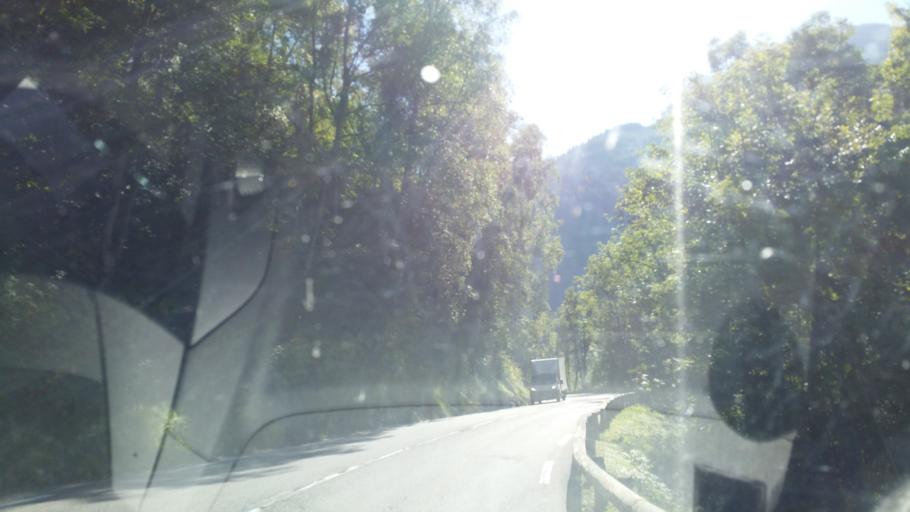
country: FR
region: Rhone-Alpes
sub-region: Departement de la Savoie
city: Seez
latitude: 45.5835
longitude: 6.8847
